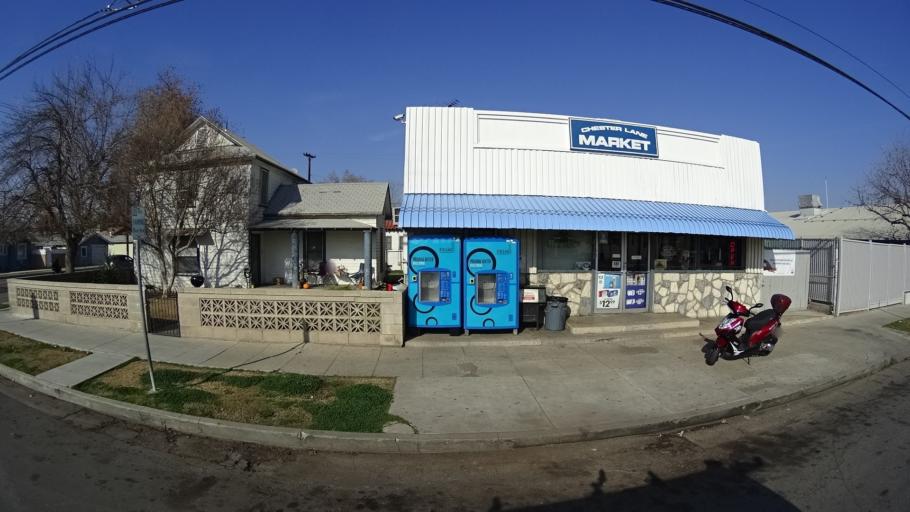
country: US
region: California
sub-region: Kern County
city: Bakersfield
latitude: 35.3649
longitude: -119.0291
